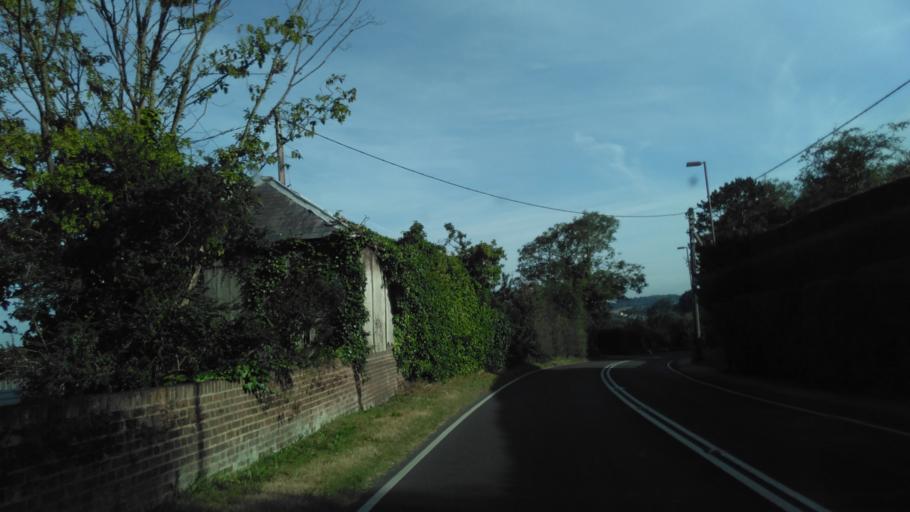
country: GB
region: England
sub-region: Kent
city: Blean
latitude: 51.3123
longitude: 1.0355
